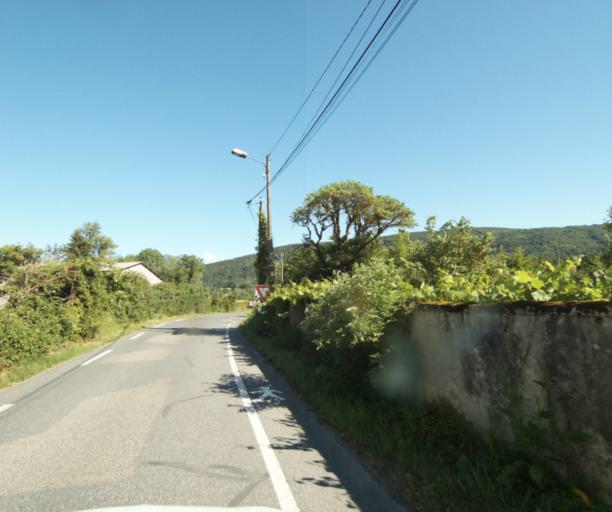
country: FR
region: Rhone-Alpes
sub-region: Departement de la Haute-Savoie
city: Sciez
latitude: 46.3277
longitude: 6.3579
